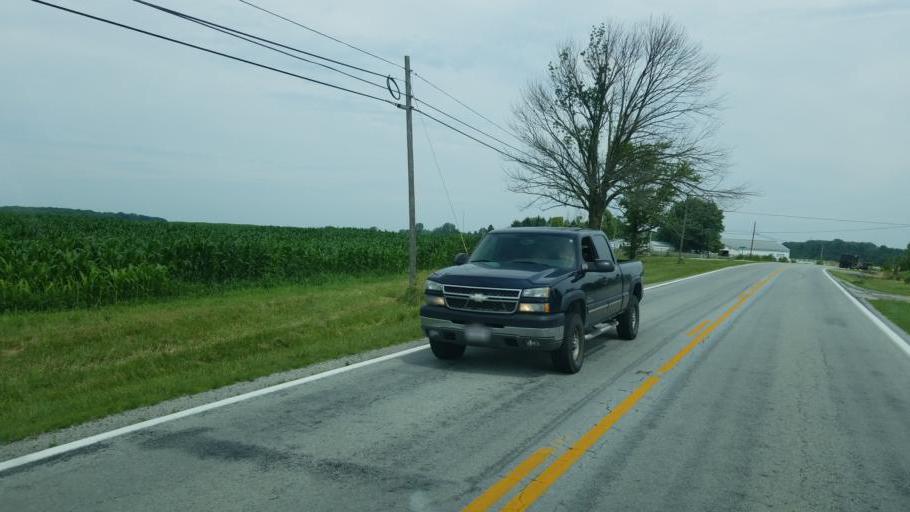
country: US
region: Ohio
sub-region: Madison County
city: Choctaw Lake
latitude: 39.9992
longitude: -83.4198
